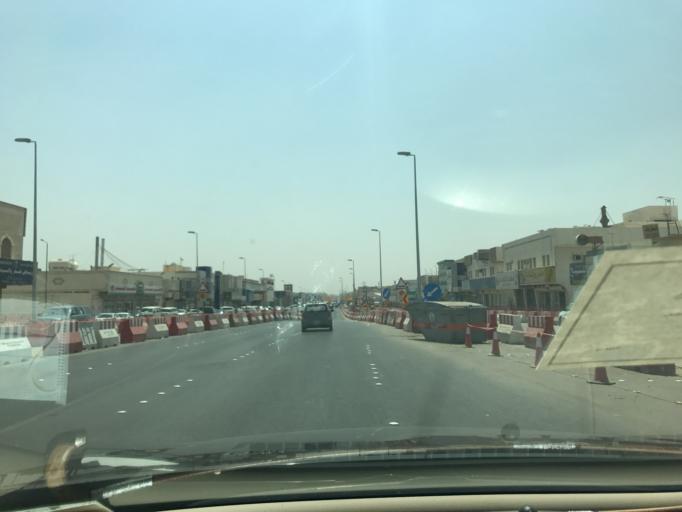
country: SA
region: Ar Riyad
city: Riyadh
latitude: 24.7527
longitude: 46.7705
